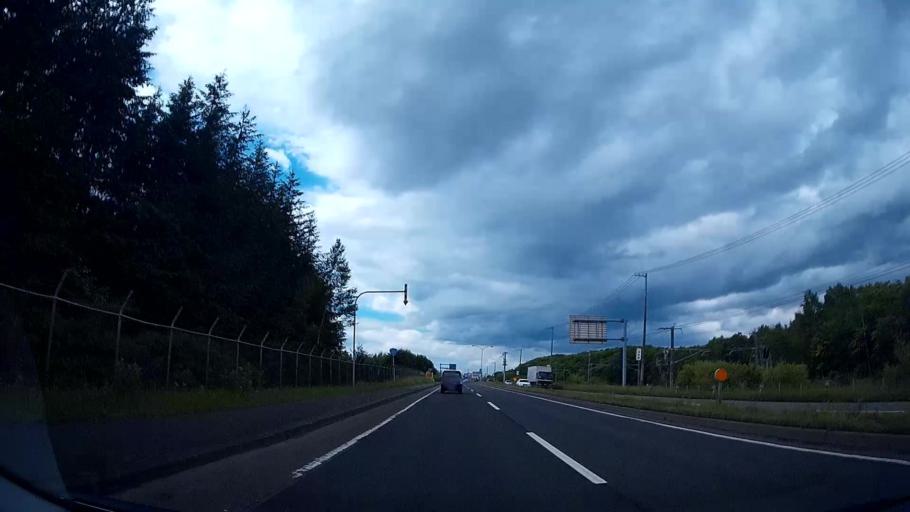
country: JP
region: Hokkaido
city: Chitose
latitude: 42.8149
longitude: 141.6667
